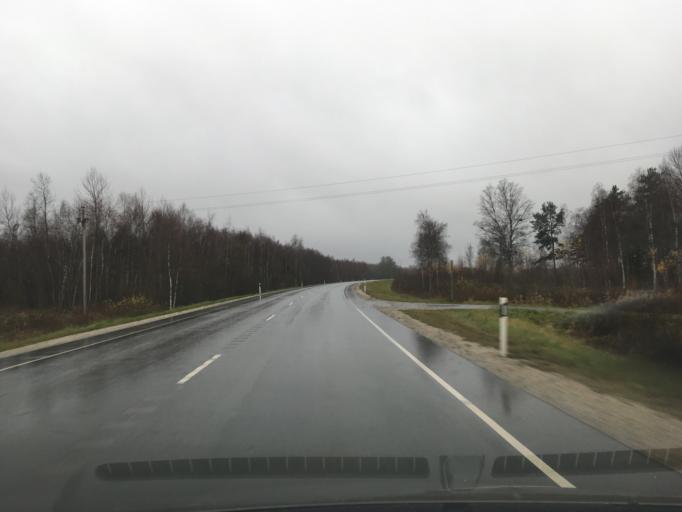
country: EE
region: Harju
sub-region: Nissi vald
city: Turba
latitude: 58.8519
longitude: 24.0691
